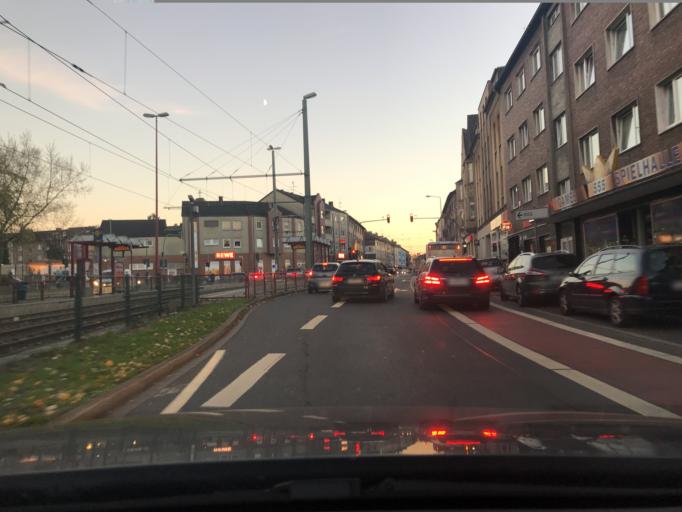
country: DE
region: North Rhine-Westphalia
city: Meiderich
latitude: 51.4801
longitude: 6.7328
